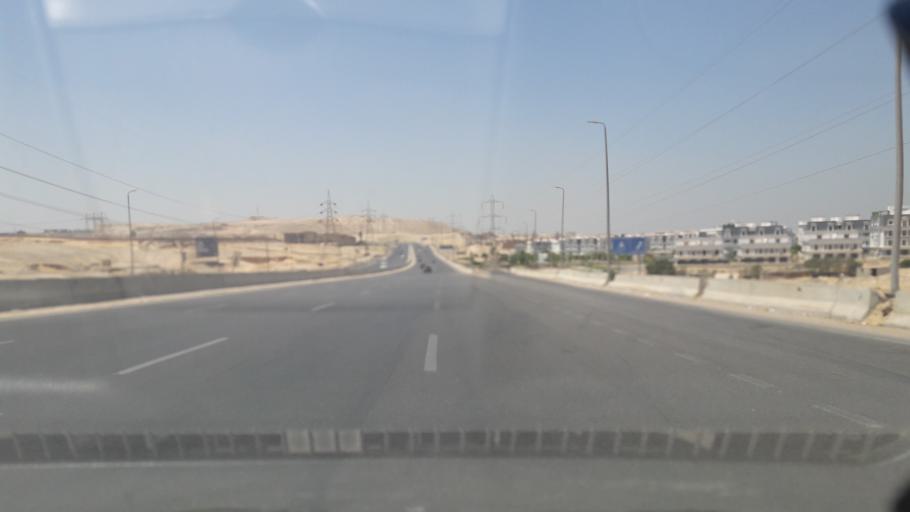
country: EG
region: Al Jizah
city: Awsim
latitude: 30.0147
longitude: 31.0842
